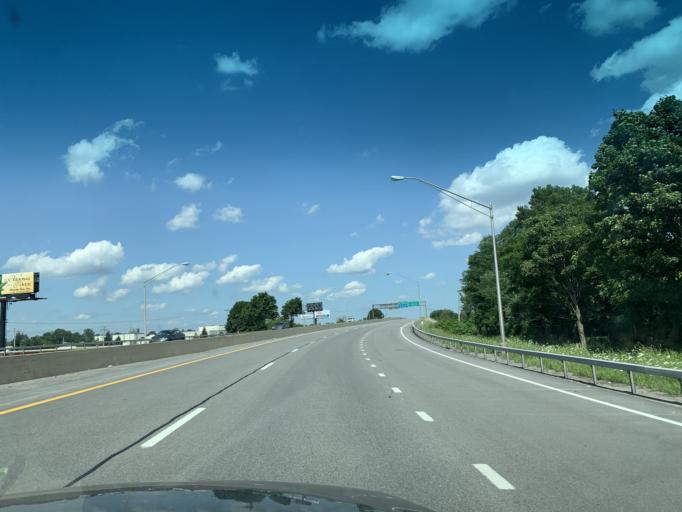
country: US
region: New York
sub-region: Oneida County
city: New Hartford
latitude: 43.0838
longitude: -75.2873
